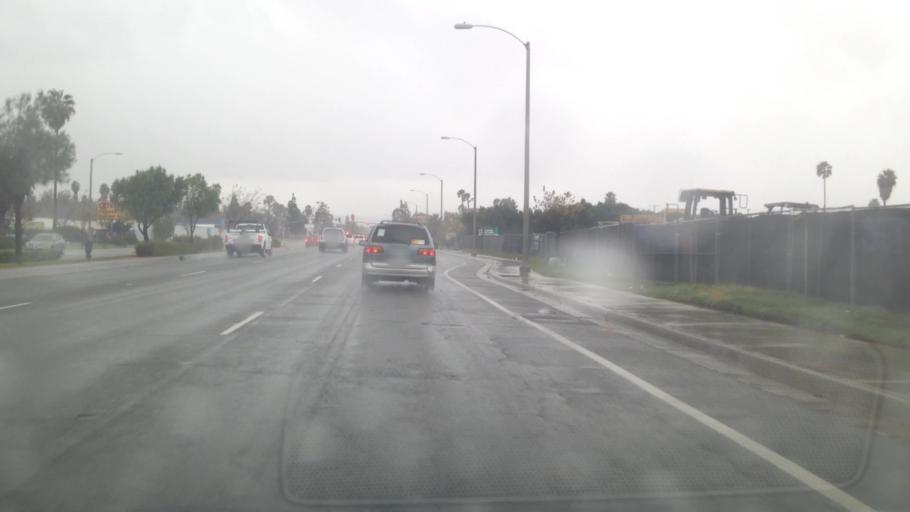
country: US
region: California
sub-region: Riverside County
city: Pedley
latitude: 33.9489
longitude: -117.4540
